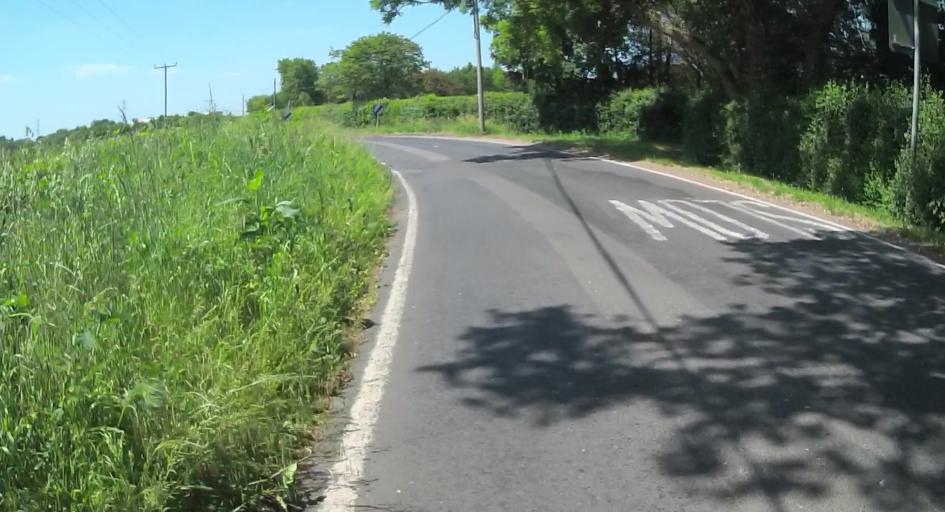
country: GB
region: England
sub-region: Hampshire
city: Tadley
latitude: 51.3171
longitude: -1.1622
